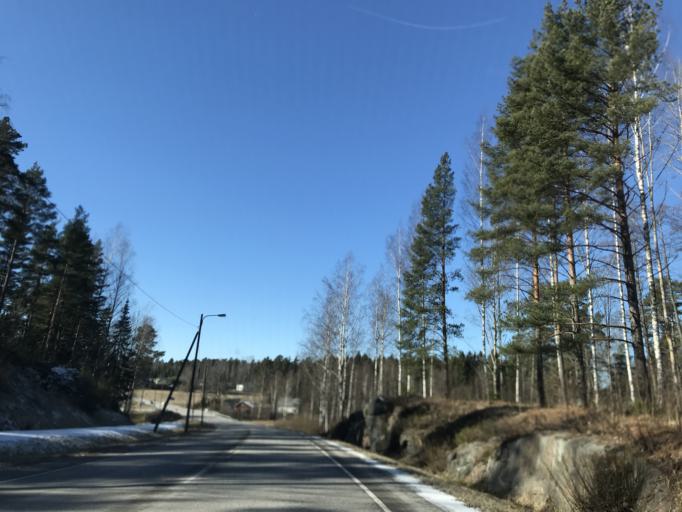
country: FI
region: Uusimaa
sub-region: Raaseporin
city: Pohja
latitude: 60.1002
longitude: 23.5293
